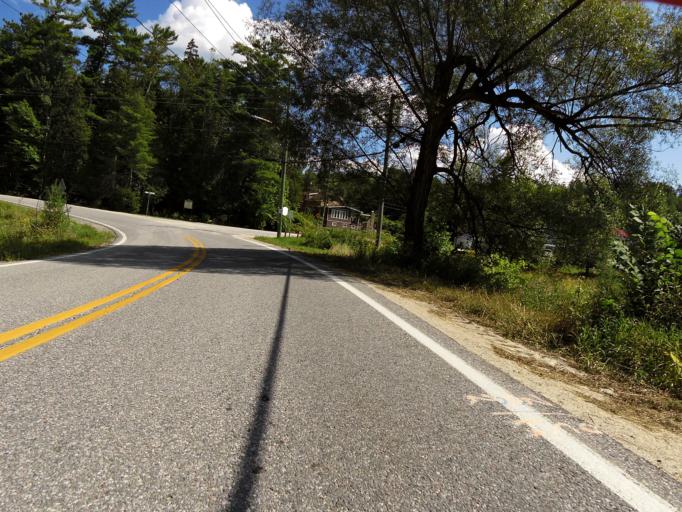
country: CA
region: Quebec
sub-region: Outaouais
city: Maniwaki
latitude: 46.1882
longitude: -76.0466
